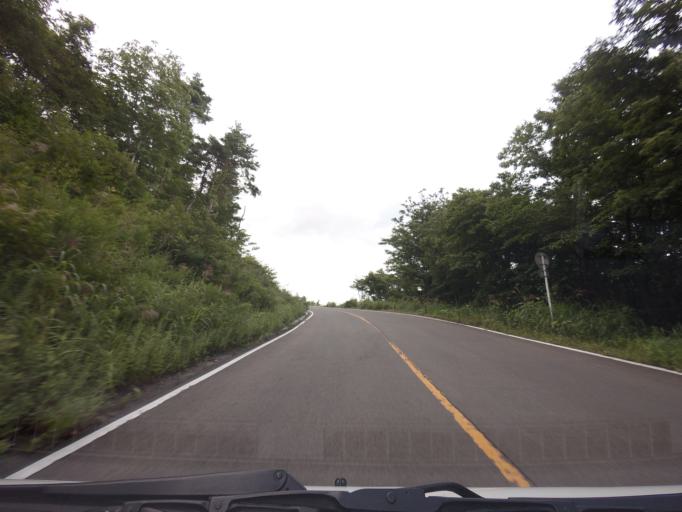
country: JP
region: Fukushima
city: Nihommatsu
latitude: 37.6222
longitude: 140.3398
